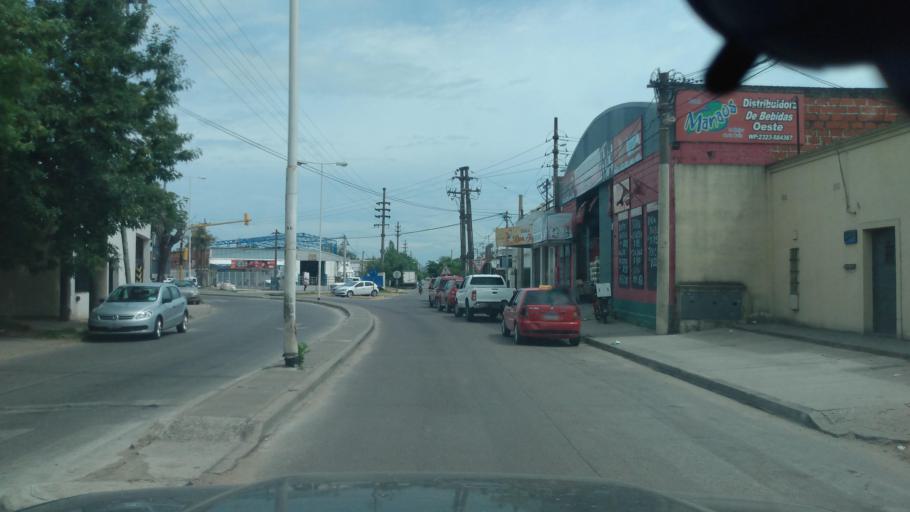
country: AR
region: Buenos Aires
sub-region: Partido de Lujan
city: Lujan
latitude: -34.5656
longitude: -59.0970
